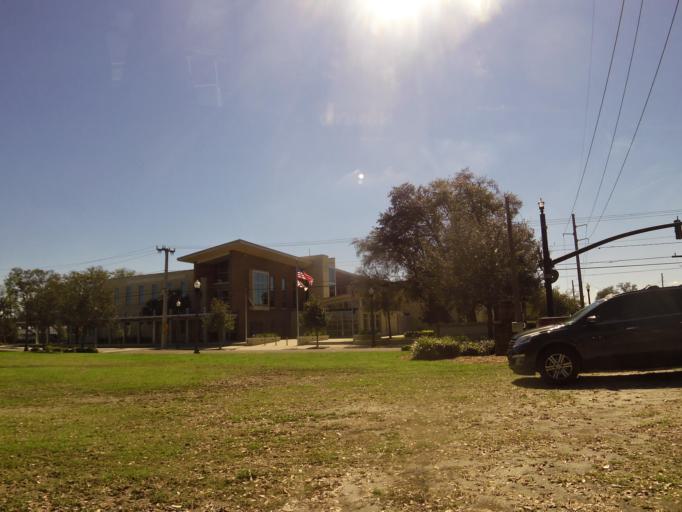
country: US
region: Florida
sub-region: Seminole County
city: Sanford
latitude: 28.8011
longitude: -81.2772
